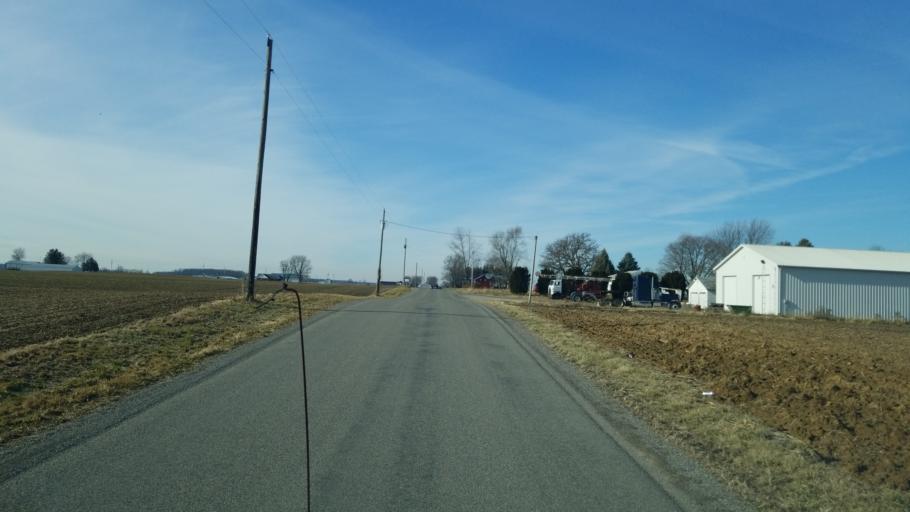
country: US
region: Ohio
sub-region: Putnam County
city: Leipsic
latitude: 41.0653
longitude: -83.9894
